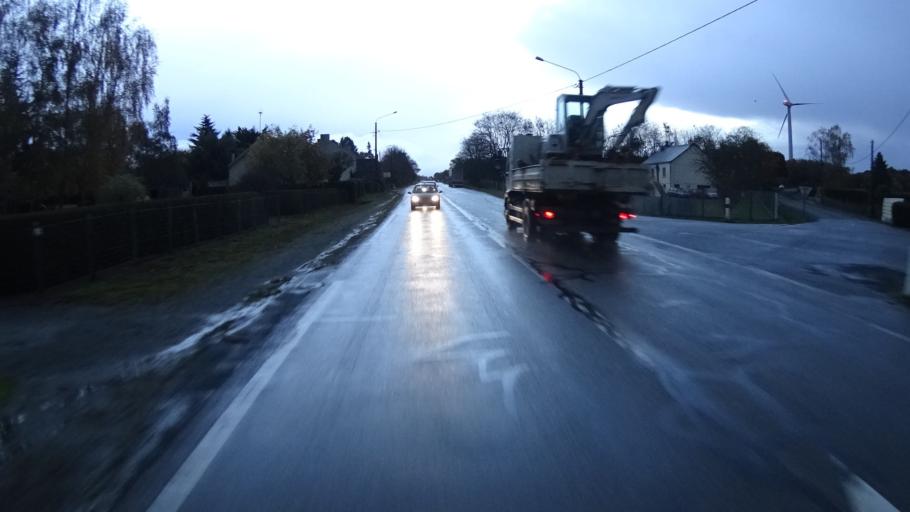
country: FR
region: Brittany
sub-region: Departement d'Ille-et-Vilaine
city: Bains-sur-Oust
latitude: 47.6801
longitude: -2.0602
